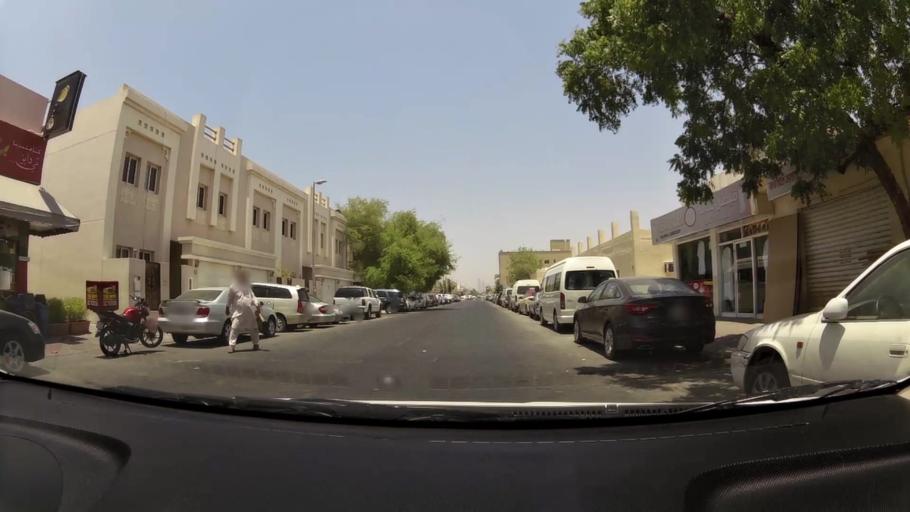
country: AE
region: Ash Shariqah
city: Sharjah
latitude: 25.2882
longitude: 55.3246
